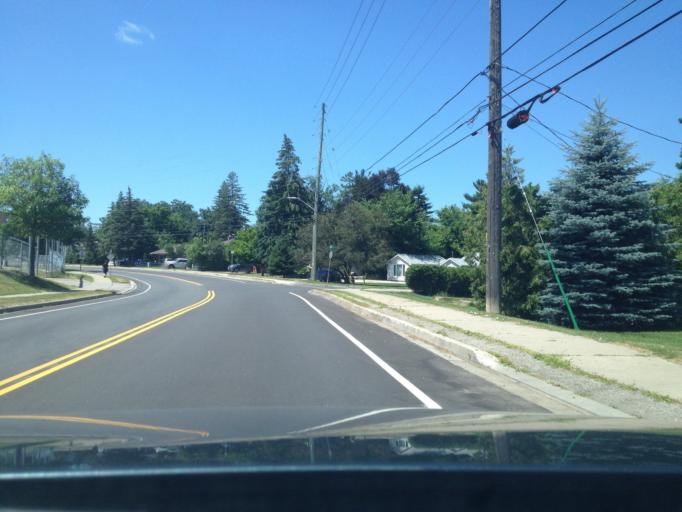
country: CA
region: Ontario
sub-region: Halton
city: Milton
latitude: 43.6604
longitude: -79.9123
